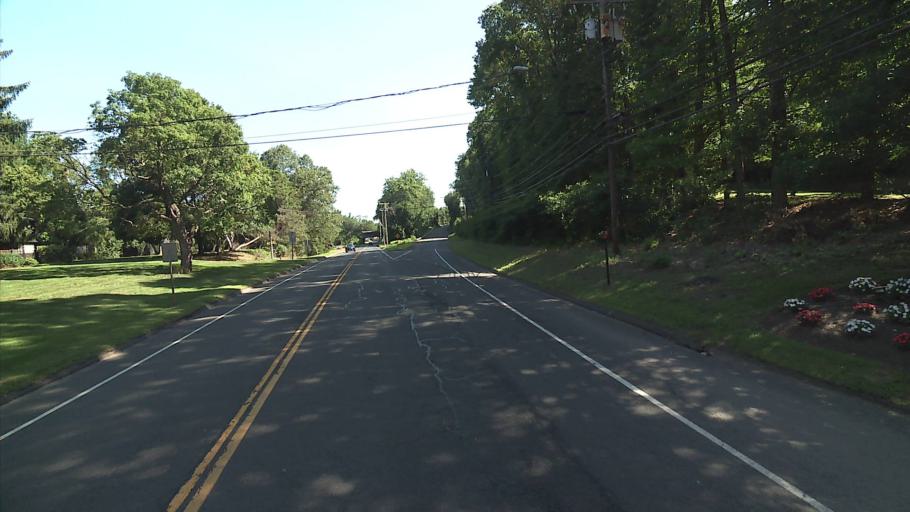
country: US
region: Connecticut
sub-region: Hartford County
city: Farmington
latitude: 41.7060
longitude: -72.8426
